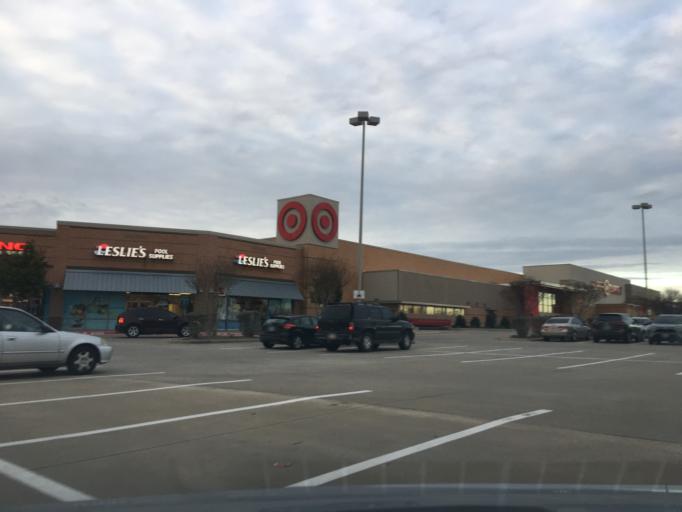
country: US
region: Texas
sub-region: Collin County
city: McKinney
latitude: 33.2194
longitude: -96.6380
